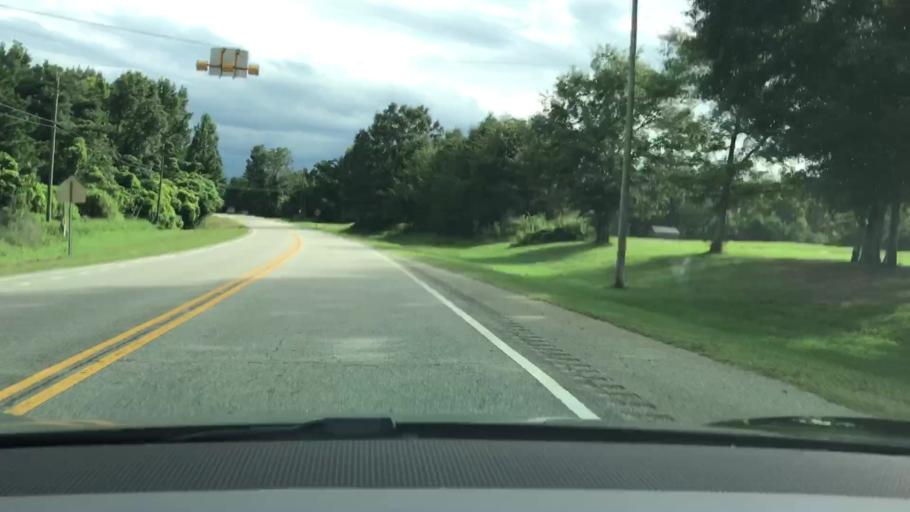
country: US
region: Alabama
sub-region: Coffee County
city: Elba
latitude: 31.5637
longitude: -86.0132
